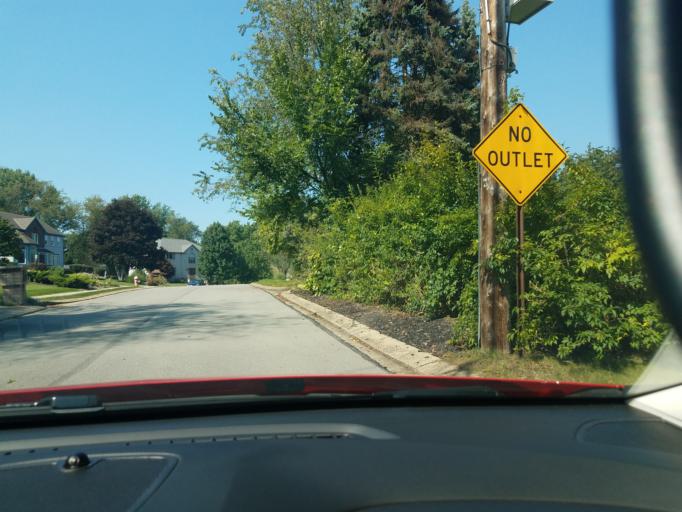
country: US
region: Pennsylvania
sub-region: Allegheny County
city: Franklin Park
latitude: 40.5651
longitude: -80.0685
